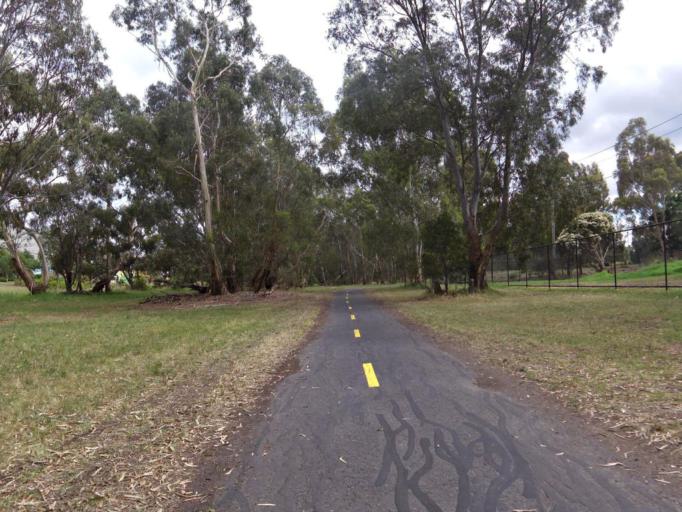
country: AU
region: Victoria
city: Heidelberg West
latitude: -37.7392
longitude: 145.0328
